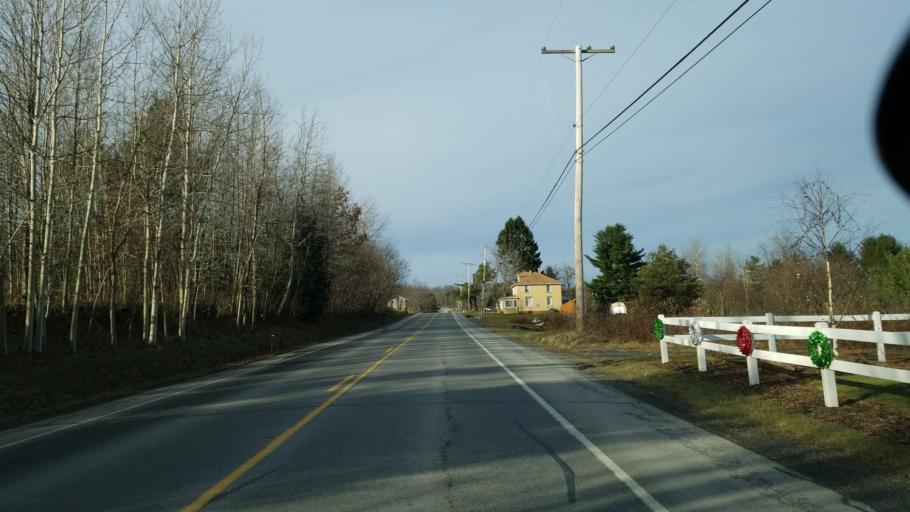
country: US
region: Pennsylvania
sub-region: Clearfield County
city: Curwensville
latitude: 41.0036
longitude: -78.6361
